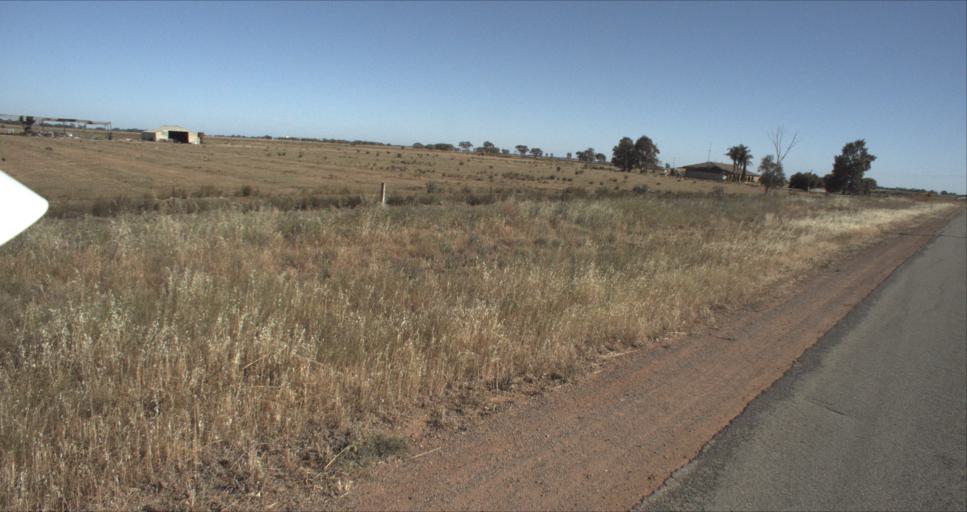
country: AU
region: New South Wales
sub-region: Leeton
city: Leeton
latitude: -34.5703
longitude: 146.3107
